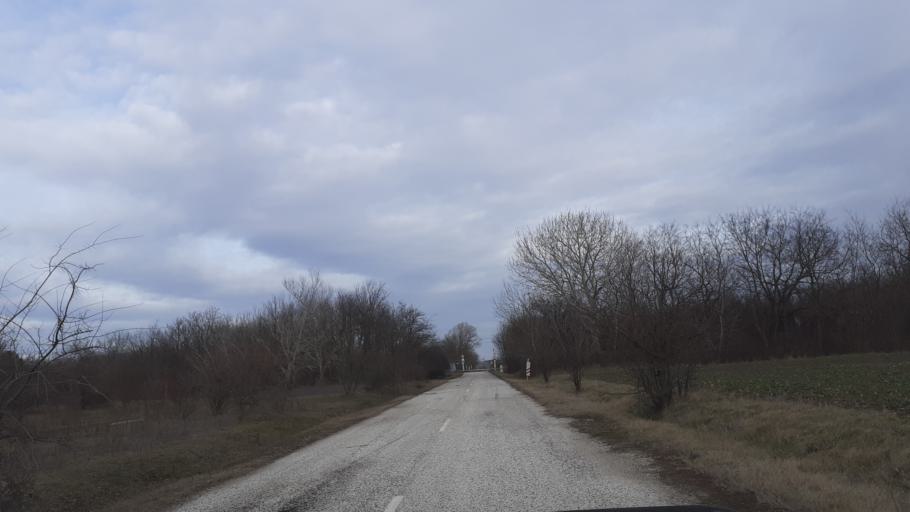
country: HU
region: Fejer
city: Szabadbattyan
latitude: 47.1210
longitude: 18.4080
